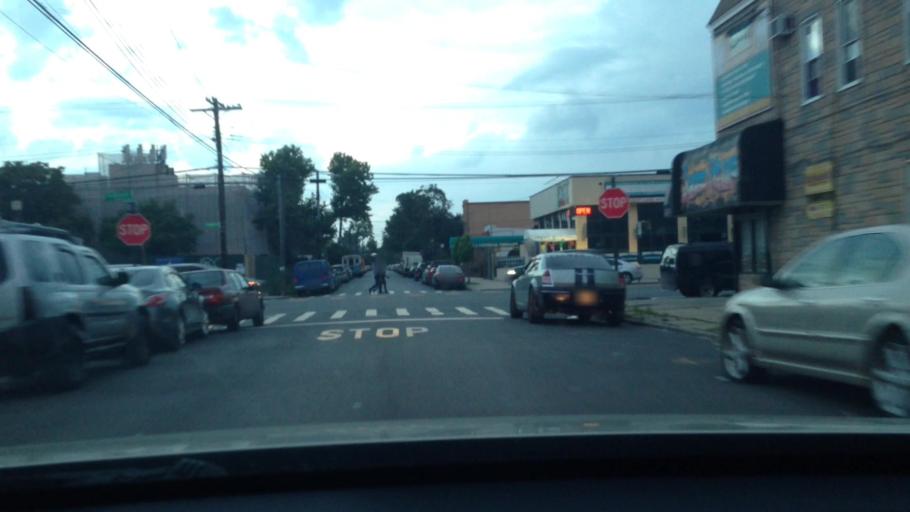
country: US
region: New York
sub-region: Kings County
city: East New York
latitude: 40.6386
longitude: -73.9079
